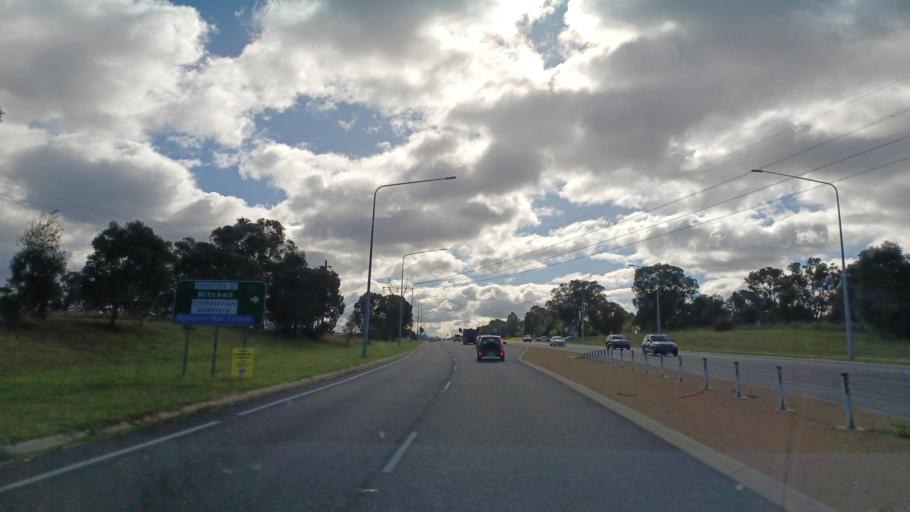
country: AU
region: Australian Capital Territory
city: Kaleen
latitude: -35.2200
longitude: 149.1302
